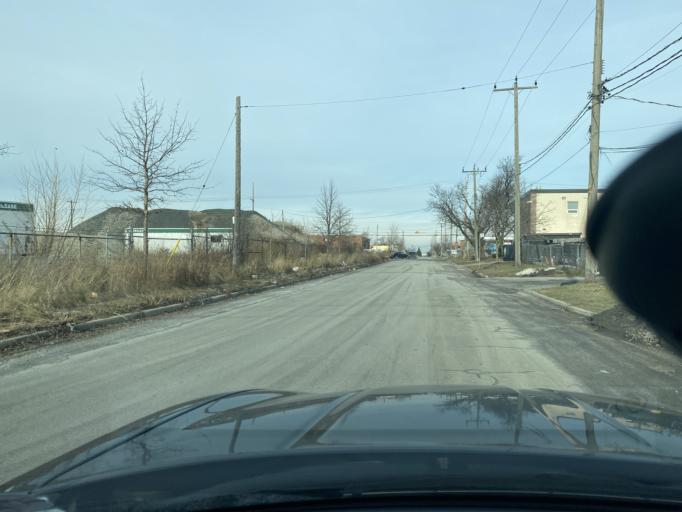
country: CA
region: Ontario
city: Scarborough
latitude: 43.7214
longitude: -79.2813
